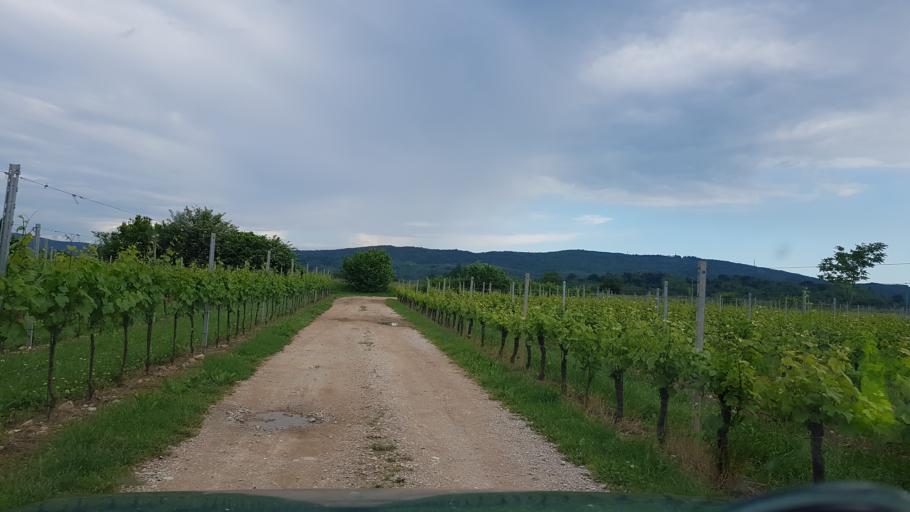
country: IT
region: Friuli Venezia Giulia
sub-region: Provincia di Gorizia
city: Mossa
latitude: 45.9187
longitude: 13.5448
